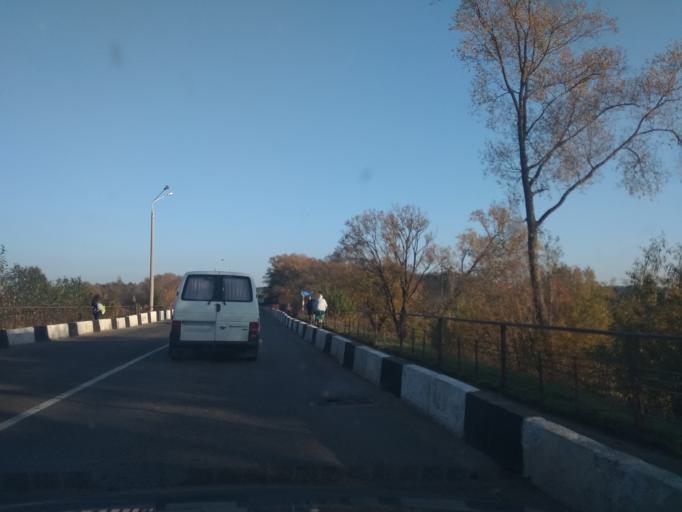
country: BY
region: Grodnenskaya
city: Vawkavysk
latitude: 53.1518
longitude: 24.4173
